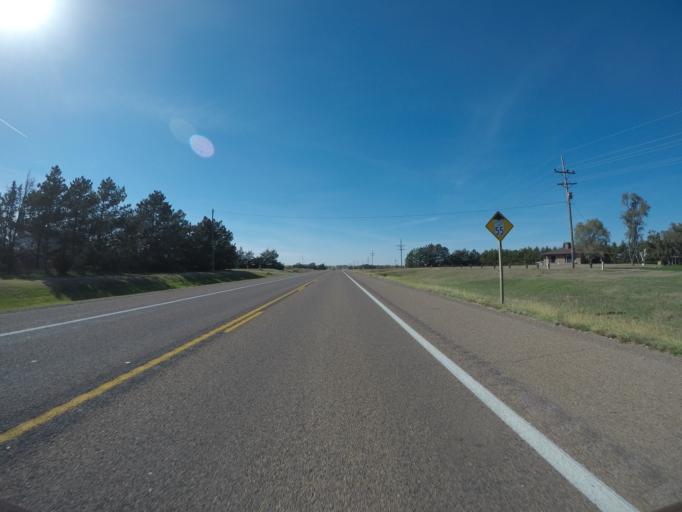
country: US
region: Kansas
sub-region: Phillips County
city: Phillipsburg
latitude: 39.7557
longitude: -99.2971
